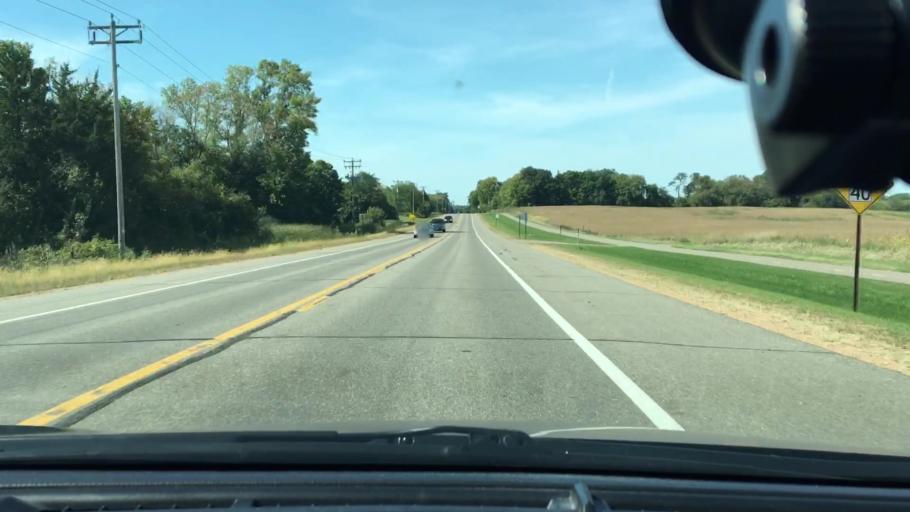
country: US
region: Minnesota
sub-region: Wright County
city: Hanover
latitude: 45.1525
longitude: -93.6511
